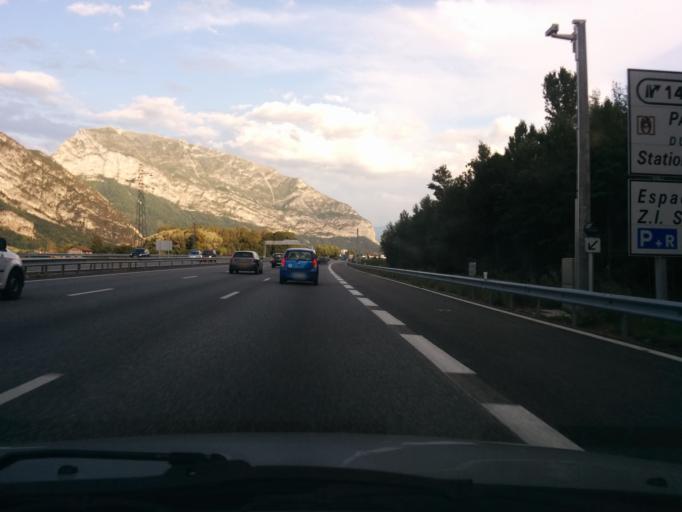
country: FR
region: Rhone-Alpes
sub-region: Departement de l'Isere
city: Noyarey
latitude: 45.2556
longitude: 5.6443
